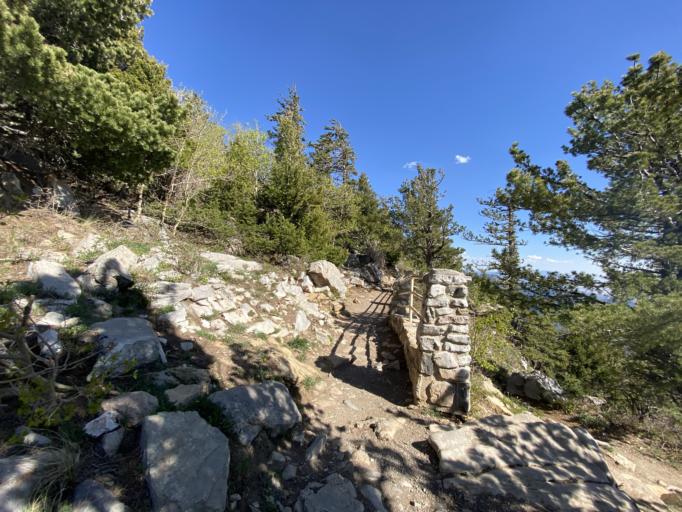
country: US
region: New Mexico
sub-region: Bernalillo County
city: Sandia Heights
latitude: 35.2081
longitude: -106.4476
